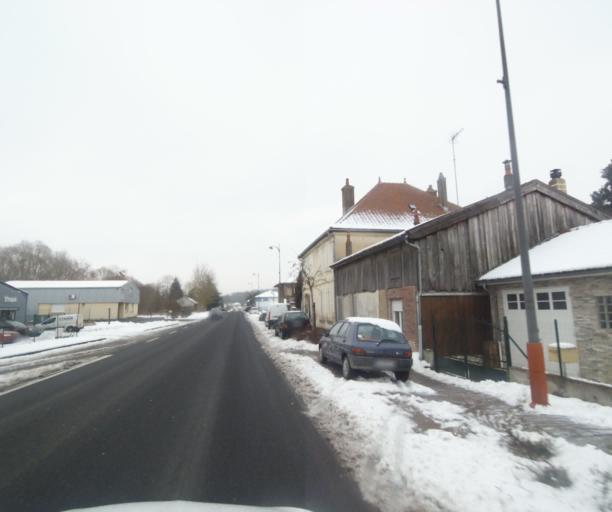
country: FR
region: Champagne-Ardenne
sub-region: Departement de la Haute-Marne
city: Villiers-en-Lieu
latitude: 48.6185
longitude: 4.9008
